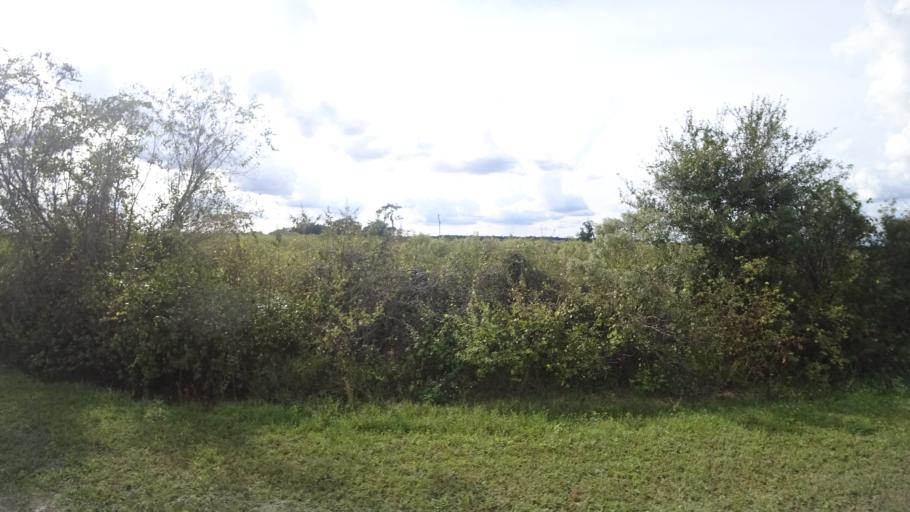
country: US
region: Florida
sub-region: DeSoto County
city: Nocatee
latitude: 27.2885
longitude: -82.1053
